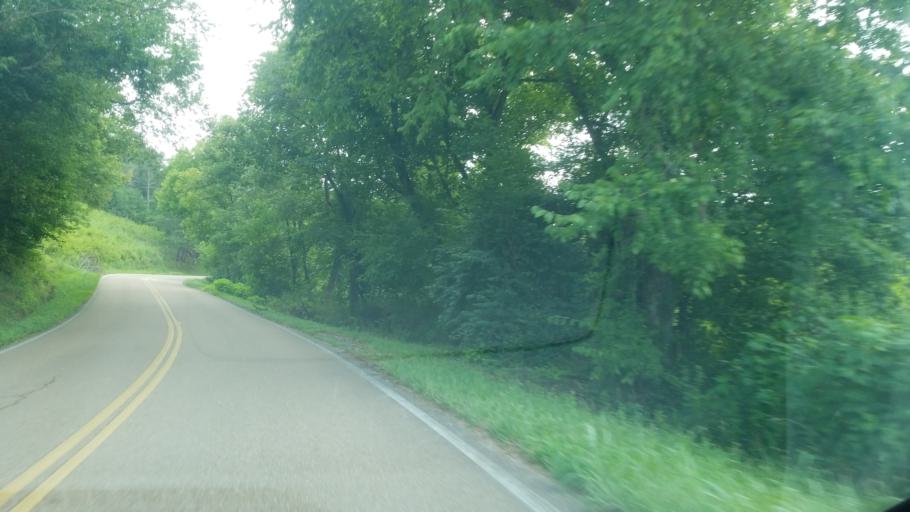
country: US
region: Tennessee
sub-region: Hamilton County
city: Lakesite
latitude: 35.2066
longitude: -85.0846
